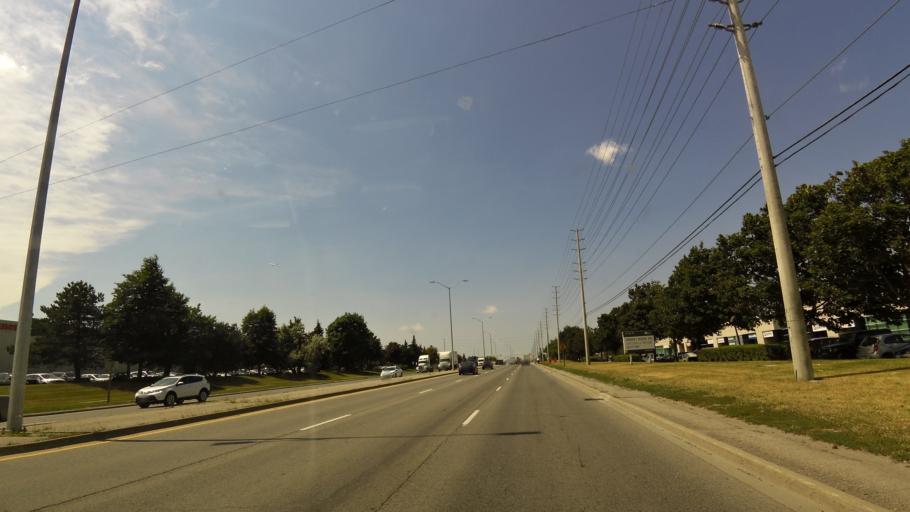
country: CA
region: Ontario
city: Mississauga
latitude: 43.6613
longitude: -79.6554
